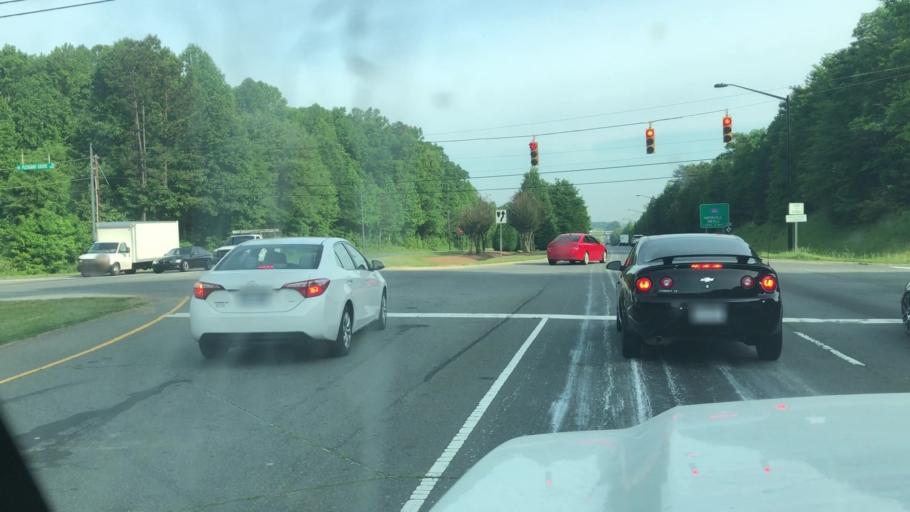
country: US
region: North Carolina
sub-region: Gaston County
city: Mount Holly
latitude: 35.3099
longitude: -80.9257
